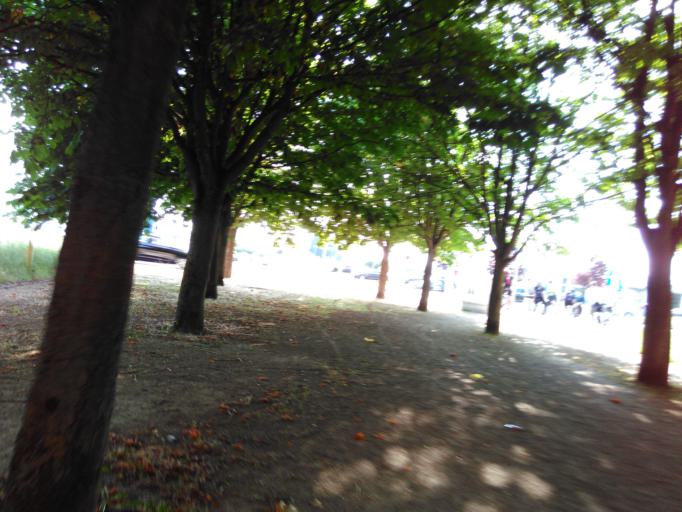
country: LU
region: Luxembourg
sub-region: Canton d'Esch-sur-Alzette
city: Esch-sur-Alzette
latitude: 49.5102
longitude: 5.9779
